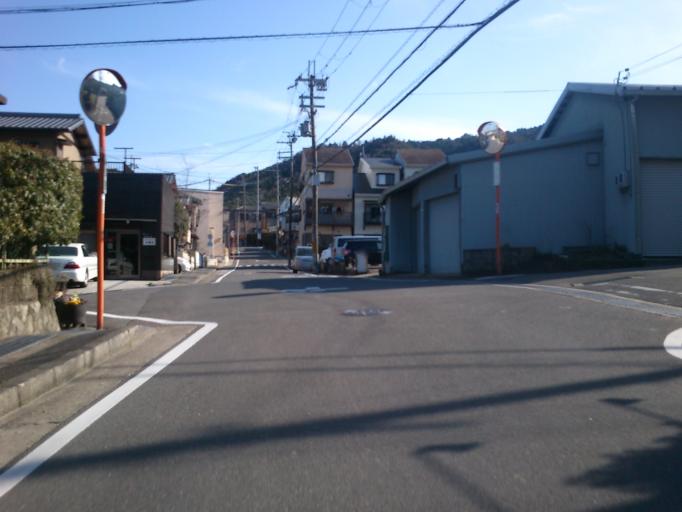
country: JP
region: Kyoto
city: Muko
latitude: 34.9184
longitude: 135.6745
